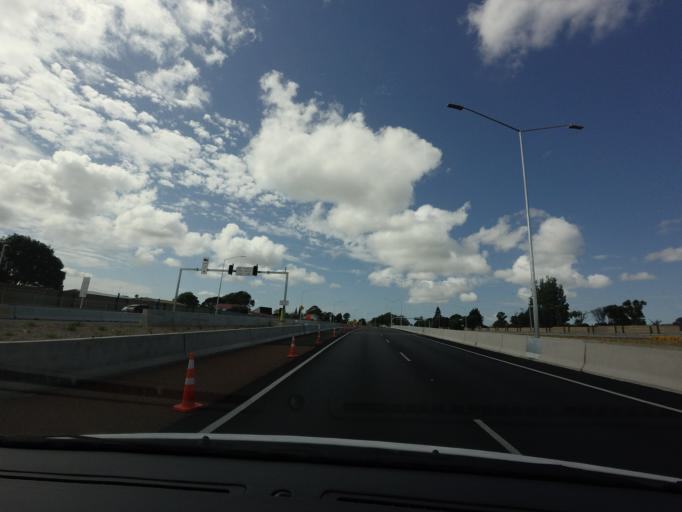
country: NZ
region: Auckland
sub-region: Auckland
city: Mangere
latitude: -36.9717
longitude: 174.7899
